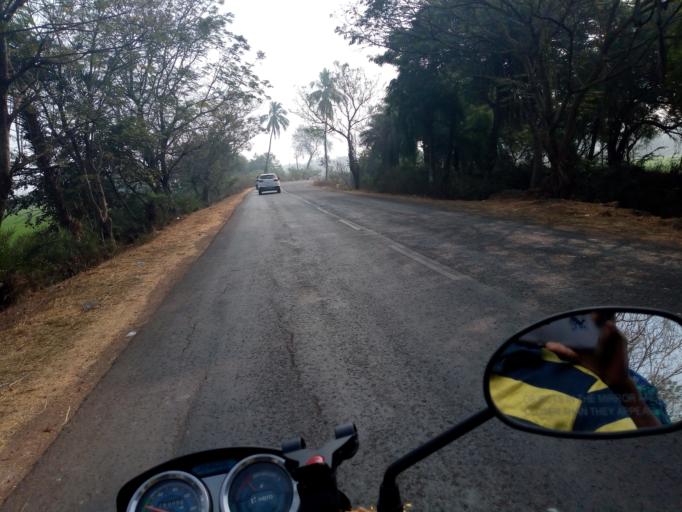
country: IN
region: Andhra Pradesh
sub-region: West Godavari
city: Tadepallegudem
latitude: 16.8004
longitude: 81.4119
